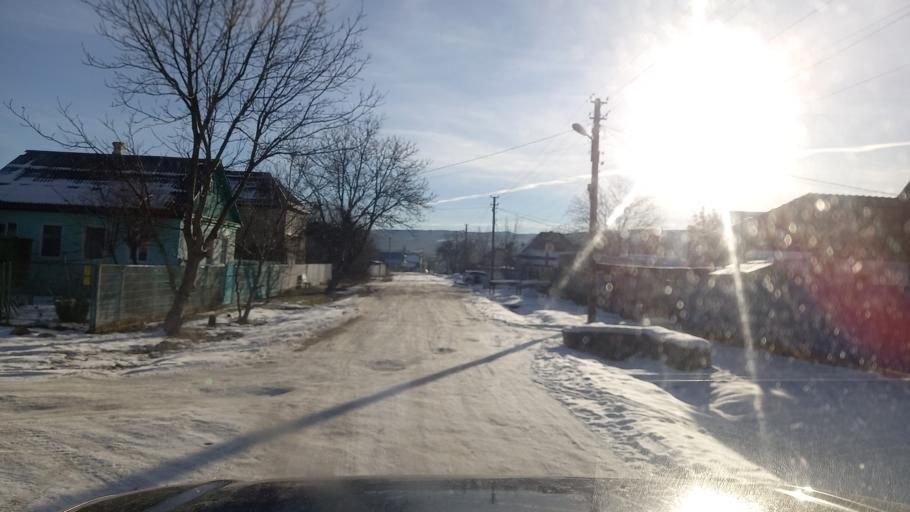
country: RU
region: Adygeya
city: Kamennomostskiy
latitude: 44.3002
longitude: 40.1684
